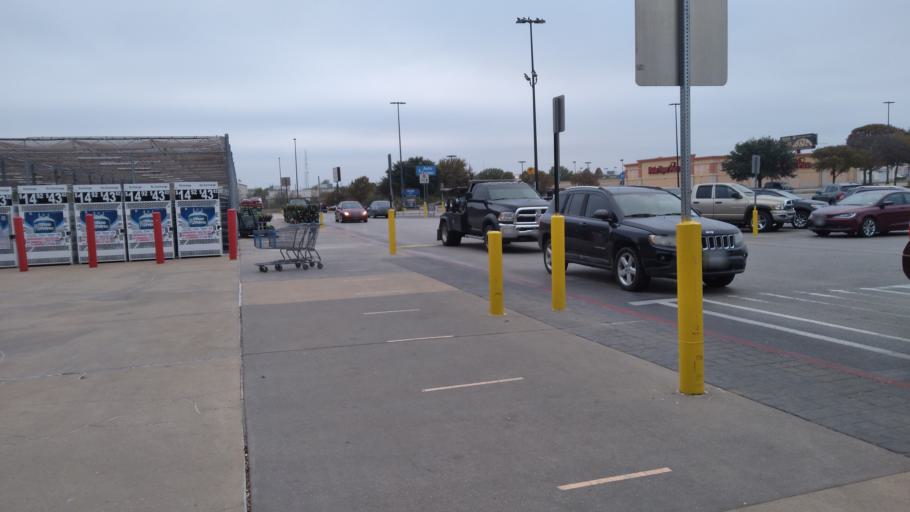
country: US
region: Texas
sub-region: McLennan County
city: Beverly Hills
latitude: 31.5217
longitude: -97.1661
